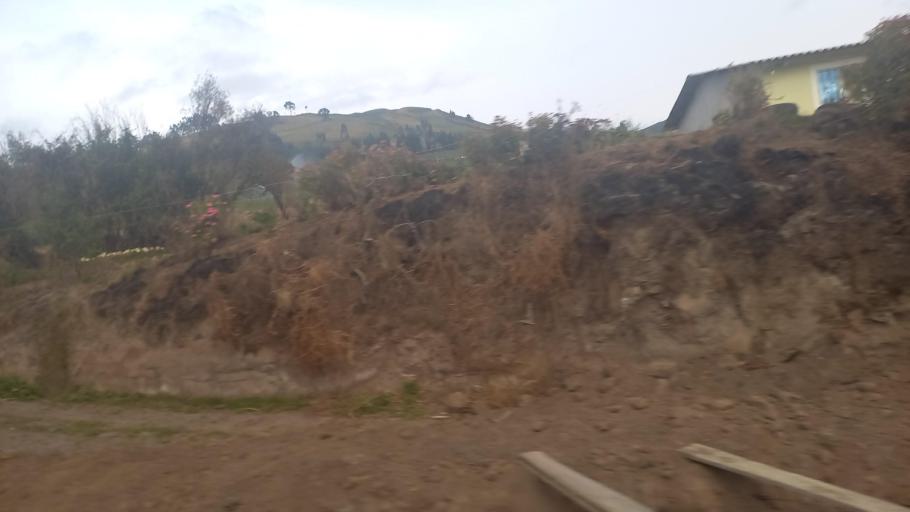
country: EC
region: Pichincha
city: Cayambe
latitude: 0.1166
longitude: -78.0776
